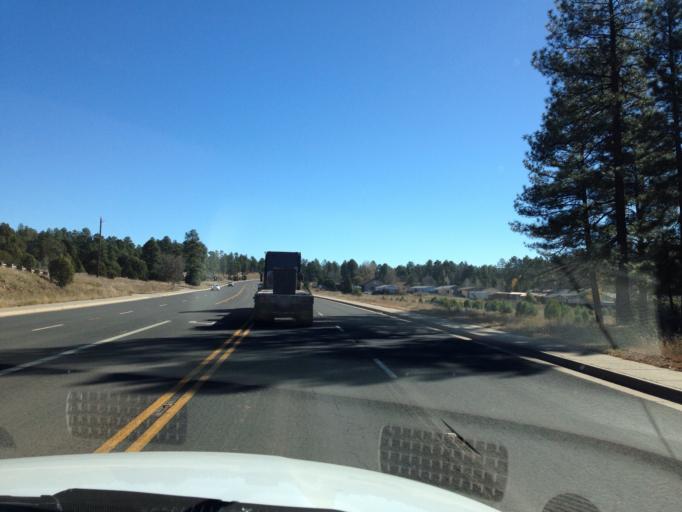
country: US
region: Arizona
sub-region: Navajo County
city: Show Low
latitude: 34.2447
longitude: -110.0672
